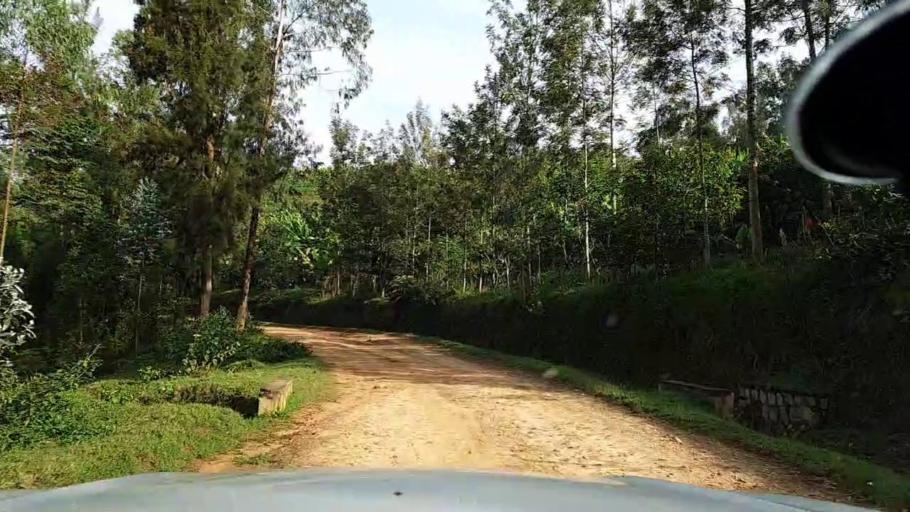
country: RW
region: Southern Province
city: Gitarama
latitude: -2.1638
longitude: 29.5538
